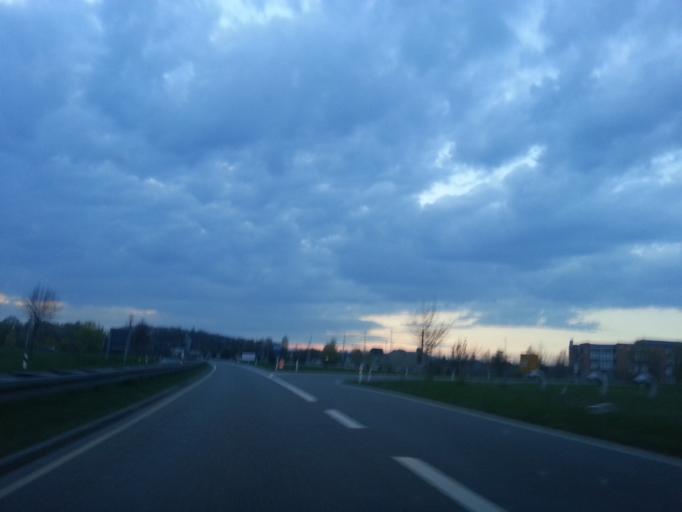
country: DE
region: Baden-Wuerttemberg
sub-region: Tuebingen Region
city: Friedrichshafen
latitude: 47.6650
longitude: 9.4932
